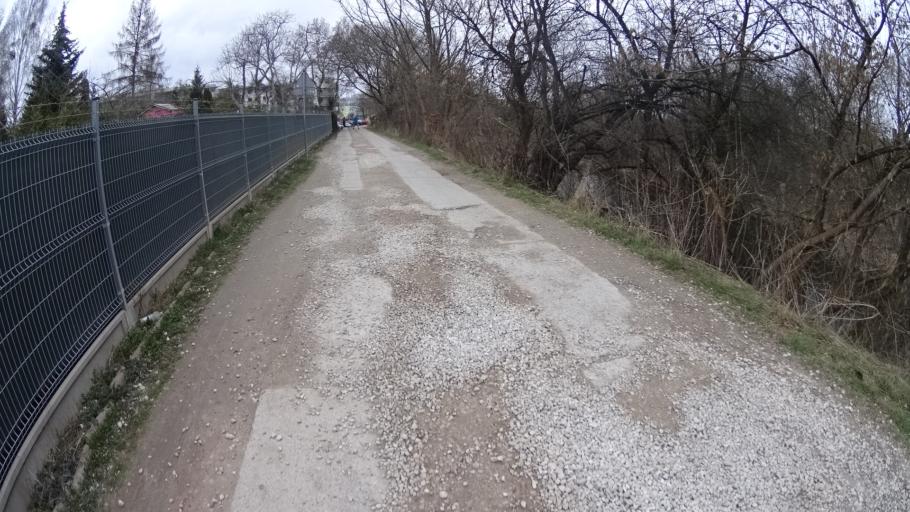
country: PL
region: Masovian Voivodeship
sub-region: Warszawa
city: Bemowo
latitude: 52.2480
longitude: 20.8931
